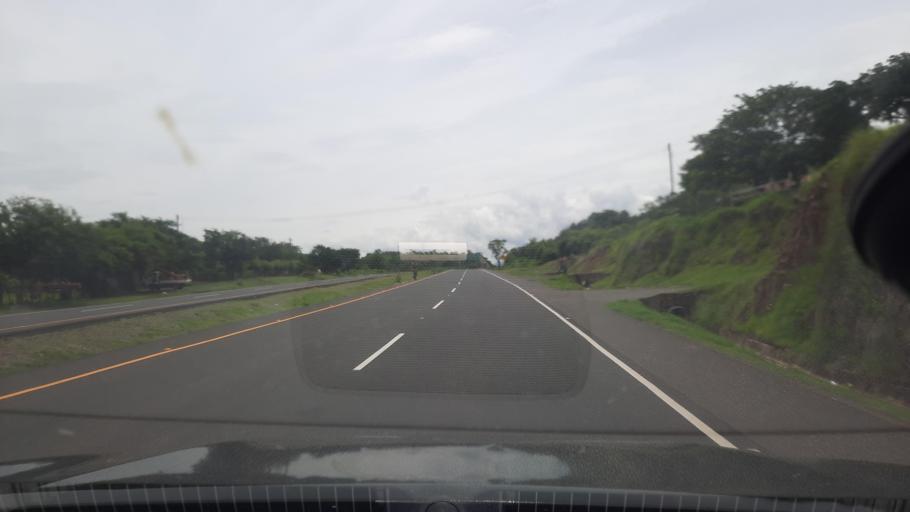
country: HN
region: Valle
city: Aramecina
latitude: 13.6763
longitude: -87.7314
